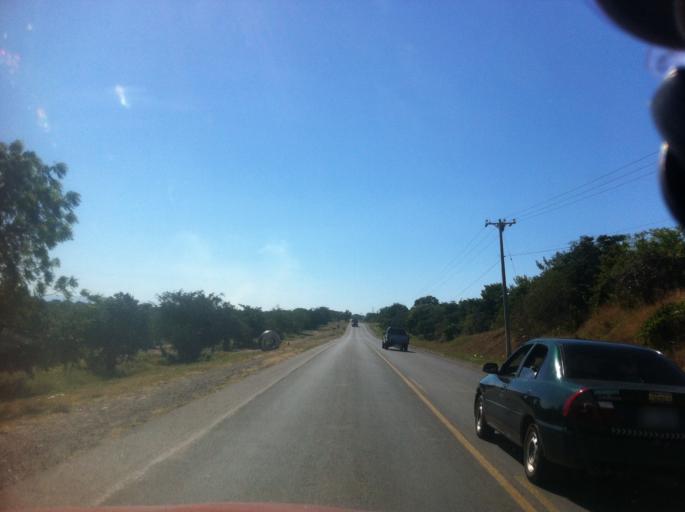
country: NI
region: Boaco
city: Teustepe
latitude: 12.3277
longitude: -85.9600
